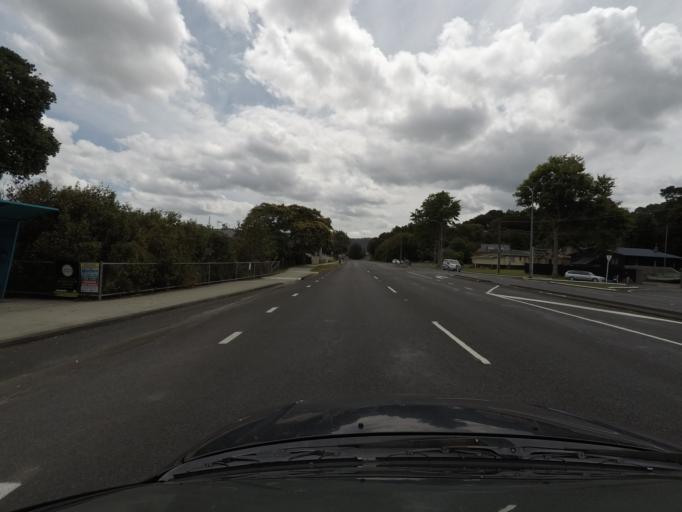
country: NZ
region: Northland
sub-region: Whangarei
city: Whangarei
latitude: -35.7282
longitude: 174.3361
